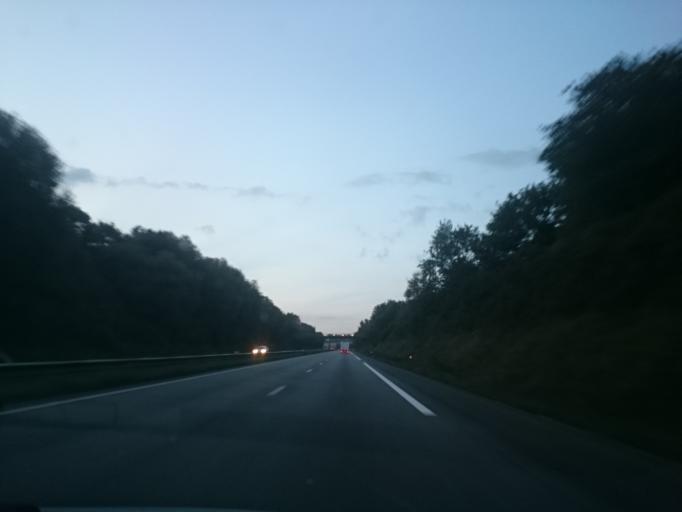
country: FR
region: Brittany
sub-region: Departement du Finistere
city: Le Faou
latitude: 48.2709
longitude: -4.1176
